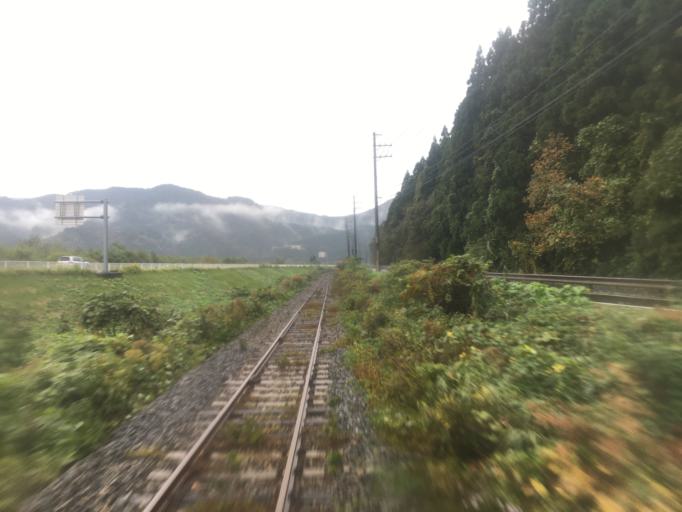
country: JP
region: Yamagata
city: Tsuruoka
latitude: 38.7903
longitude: 140.0036
